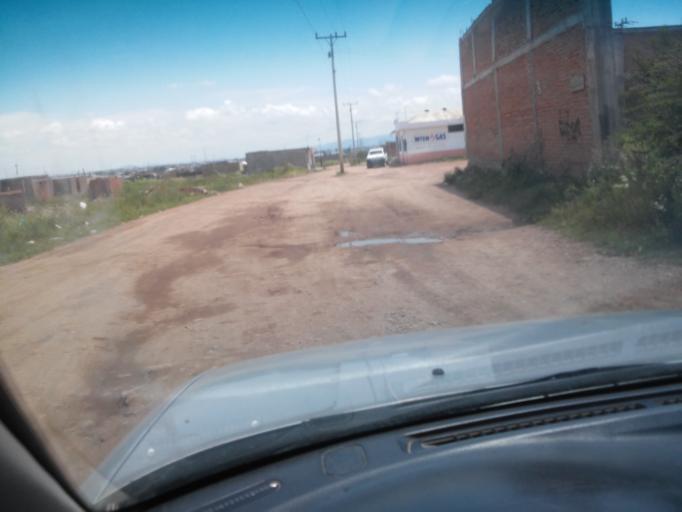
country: MX
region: Durango
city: Victoria de Durango
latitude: 23.9839
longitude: -104.7051
